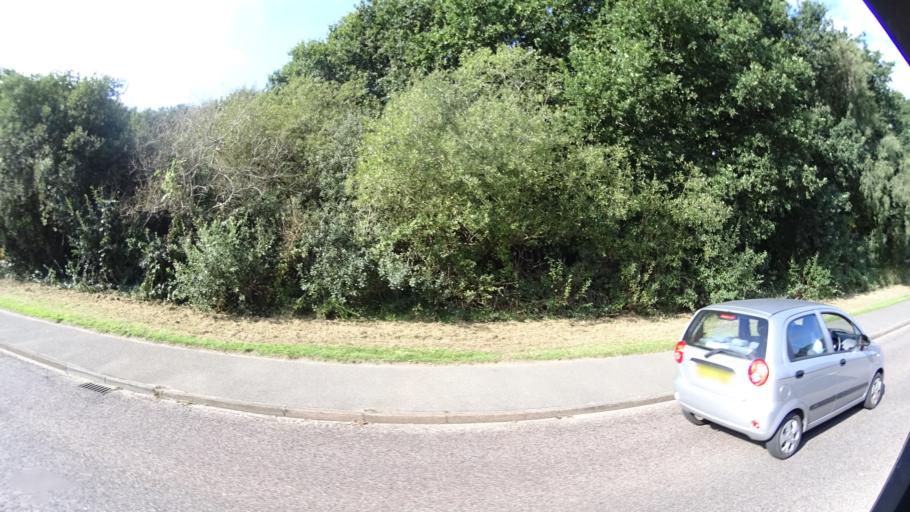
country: GB
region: England
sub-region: Dorset
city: Parkstone
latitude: 50.7573
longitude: -1.9204
